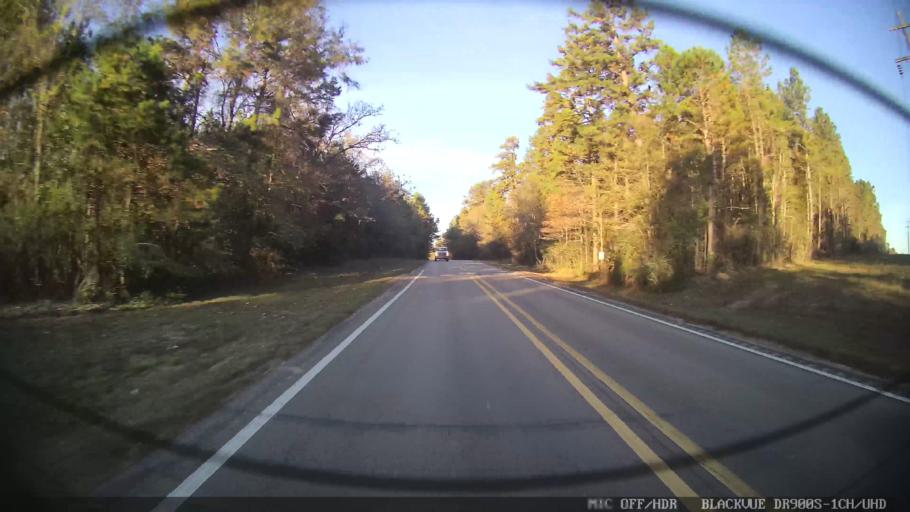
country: US
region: Mississippi
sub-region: Lamar County
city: Lumberton
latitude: 31.0617
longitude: -89.4256
